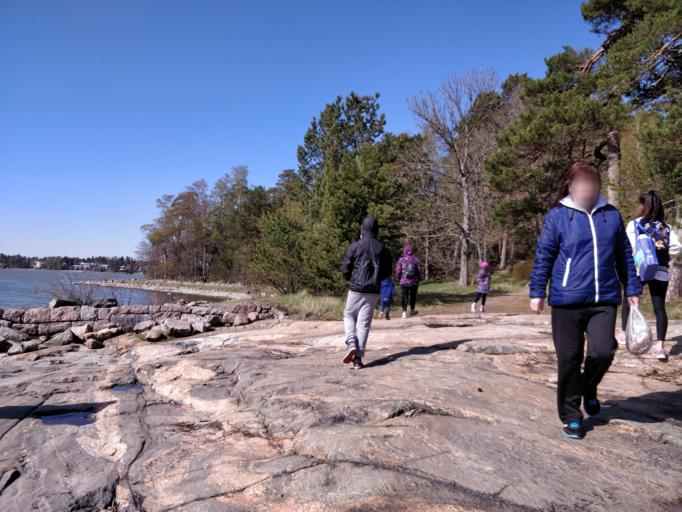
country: FI
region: Uusimaa
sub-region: Helsinki
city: Teekkarikylae
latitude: 60.1767
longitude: 24.8821
